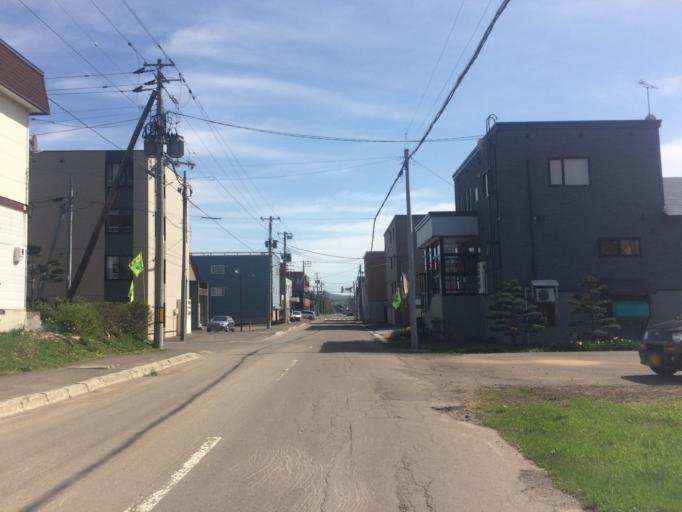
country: JP
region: Hokkaido
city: Niseko Town
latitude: 42.9049
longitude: 140.7561
